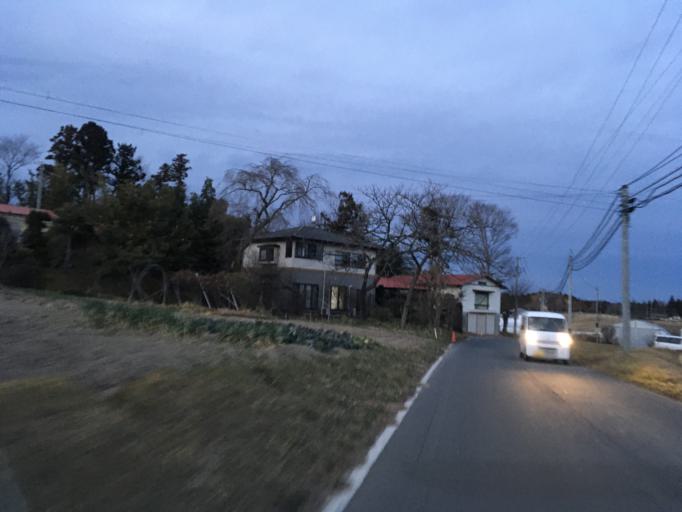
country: JP
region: Miyagi
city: Kogota
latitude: 38.6818
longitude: 141.0944
